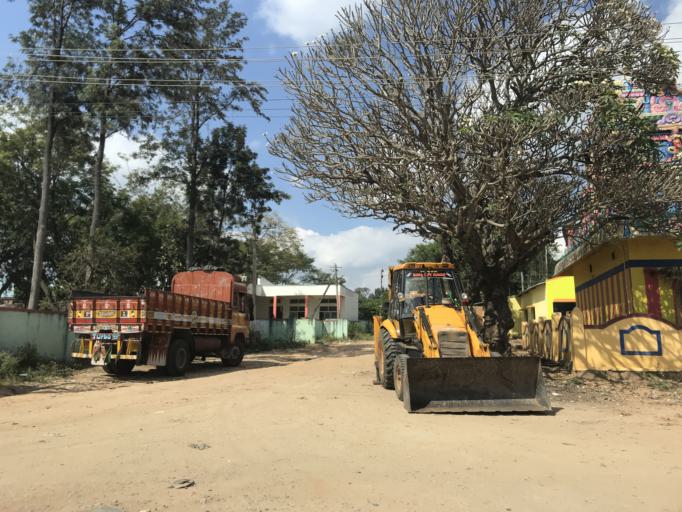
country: IN
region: Karnataka
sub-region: Hassan
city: Hassan
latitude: 12.9945
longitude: 76.0764
